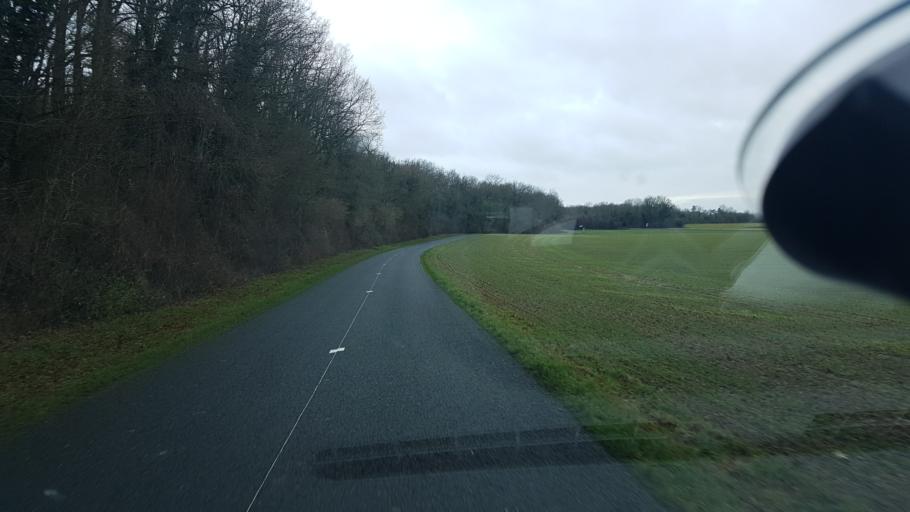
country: FR
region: Ile-de-France
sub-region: Departement de Seine-et-Marne
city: Montigny-sur-Loing
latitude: 48.2761
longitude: 2.7643
